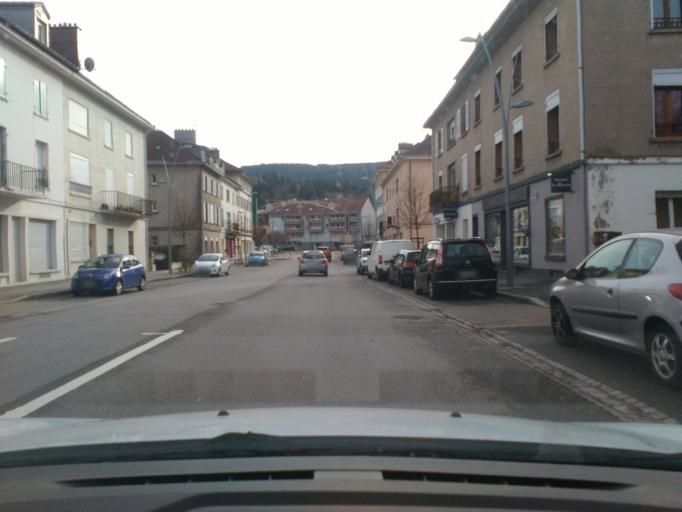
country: FR
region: Lorraine
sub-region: Departement des Vosges
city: Gerardmer
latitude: 48.0727
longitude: 6.8703
